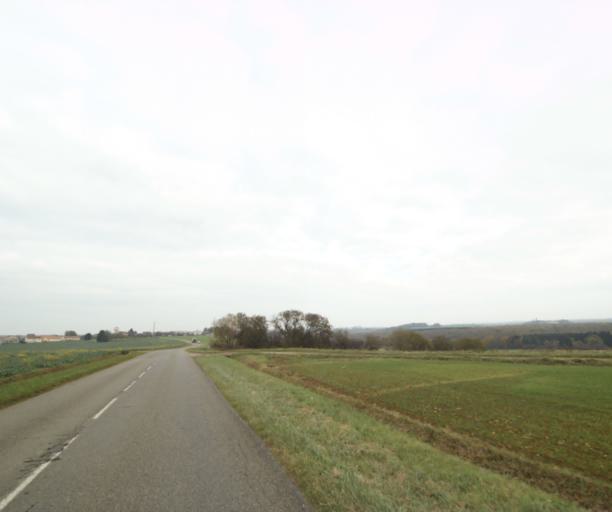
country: FR
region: Lorraine
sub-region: Departement de Meurthe-et-Moselle
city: Mancieulles
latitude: 49.2940
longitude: 5.9078
